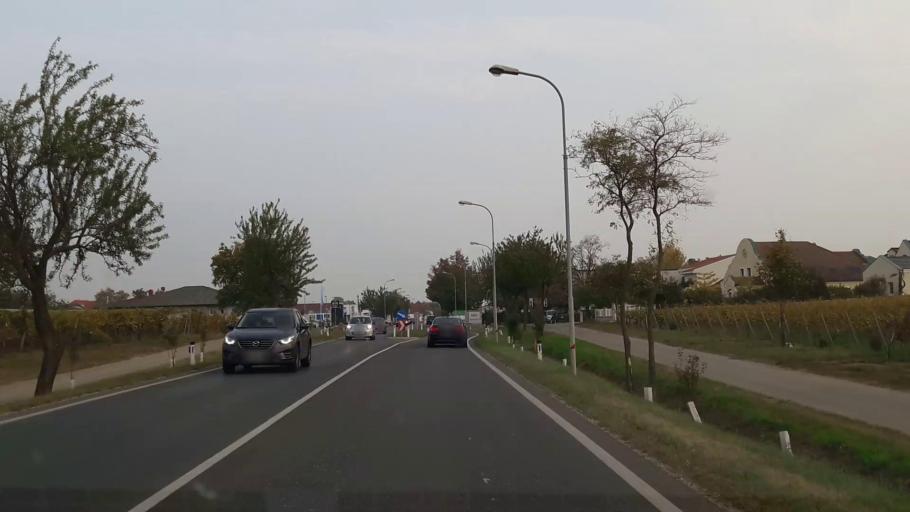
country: AT
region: Burgenland
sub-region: Politischer Bezirk Neusiedl am See
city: Gols
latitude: 47.9073
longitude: 16.8954
